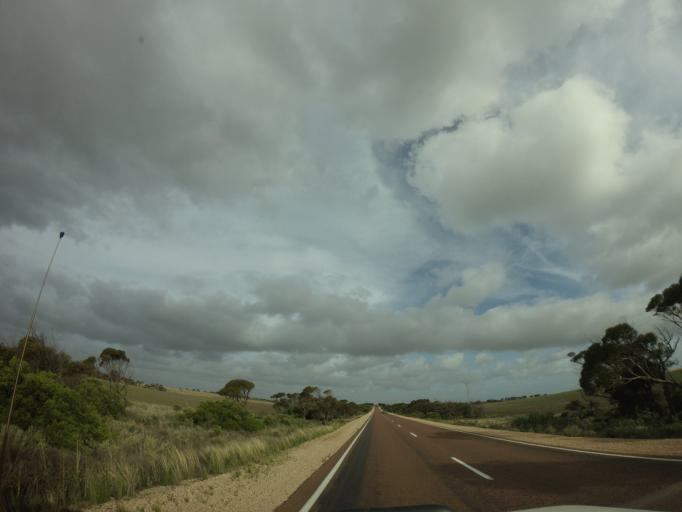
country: AU
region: South Australia
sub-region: Ceduna
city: Ceduna
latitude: -32.0360
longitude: 133.5725
